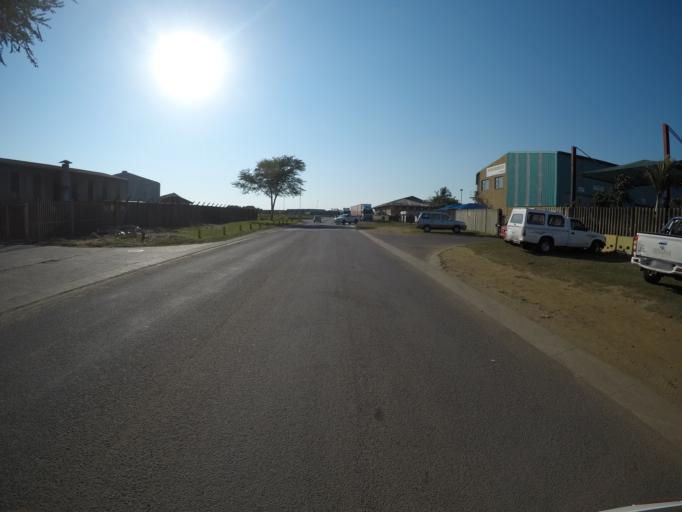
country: ZA
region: KwaZulu-Natal
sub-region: uThungulu District Municipality
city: Richards Bay
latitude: -28.7520
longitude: 32.0264
